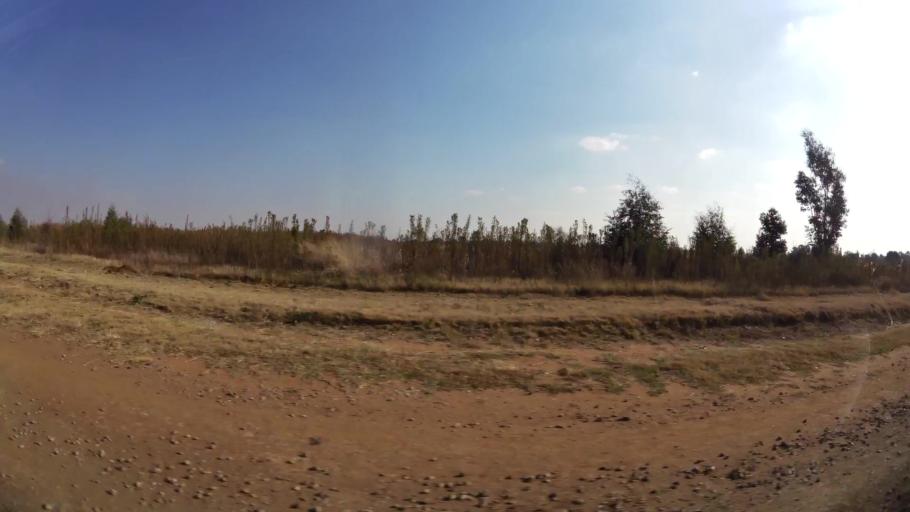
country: ZA
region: Gauteng
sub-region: Ekurhuleni Metropolitan Municipality
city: Benoni
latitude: -26.1421
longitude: 28.3936
